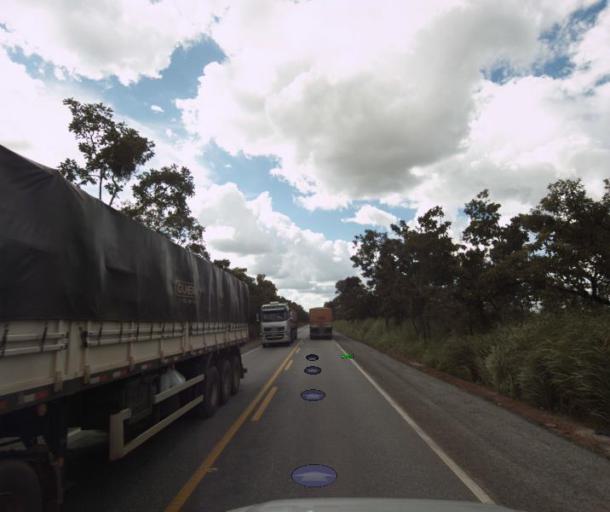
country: BR
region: Goias
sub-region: Porangatu
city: Porangatu
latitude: -13.2723
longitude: -49.1310
